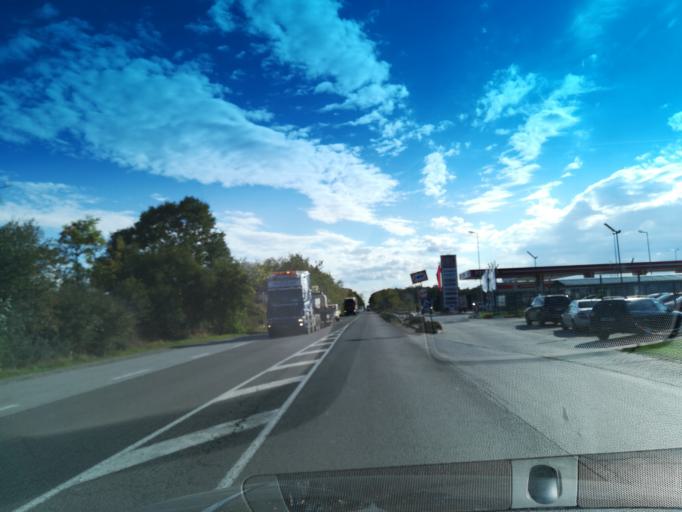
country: BG
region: Stara Zagora
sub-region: Obshtina Stara Zagora
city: Stara Zagora
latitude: 42.3569
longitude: 25.6569
